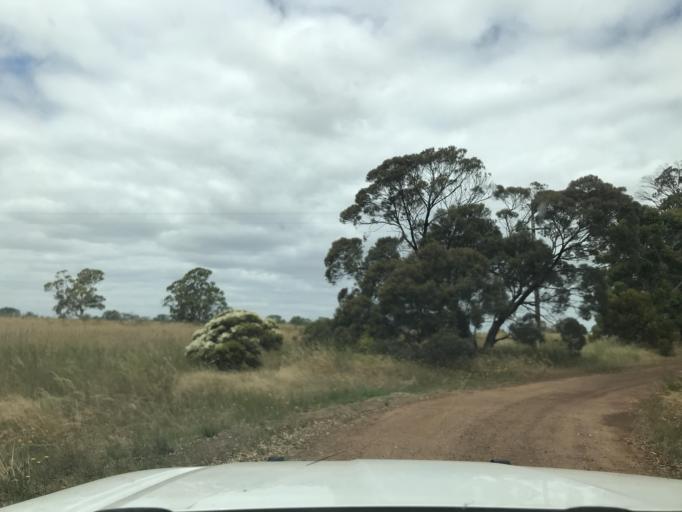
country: AU
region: South Australia
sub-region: Naracoorte and Lucindale
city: Naracoorte
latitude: -36.9967
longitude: 141.3559
